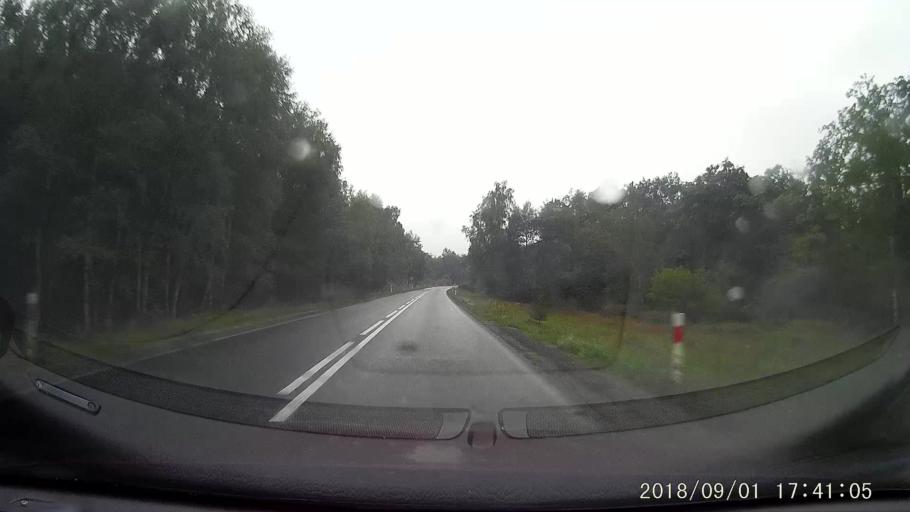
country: PL
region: Lubusz
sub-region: Powiat zaganski
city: Zagan
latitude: 51.5715
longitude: 15.2704
